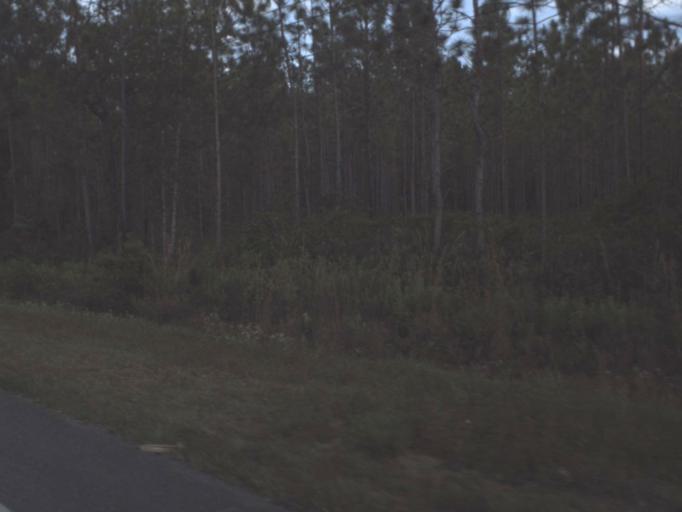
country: US
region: Florida
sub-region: Marion County
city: Silver Springs Shores
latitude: 29.2134
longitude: -81.9674
